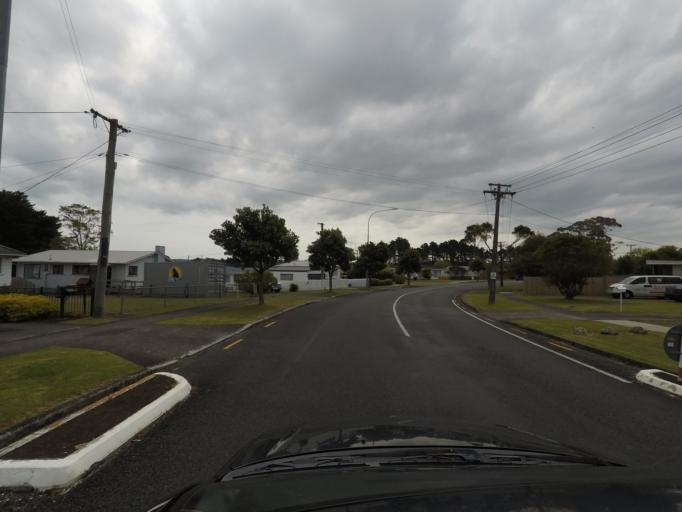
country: NZ
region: Auckland
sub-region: Auckland
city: Rosebank
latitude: -36.8497
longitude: 174.6466
